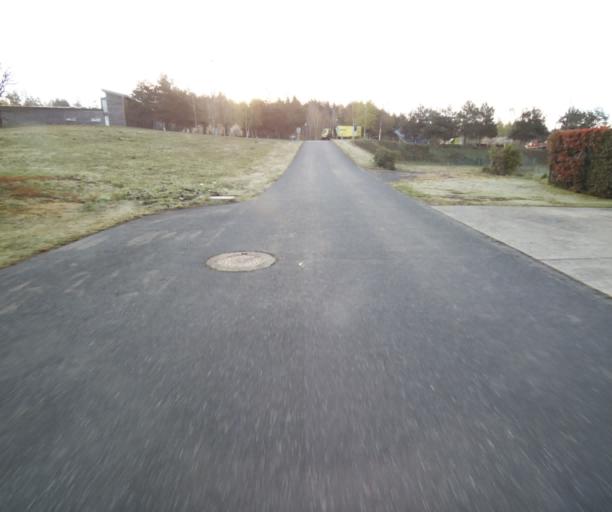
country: FR
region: Limousin
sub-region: Departement de la Correze
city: Correze
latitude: 45.3185
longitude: 1.8482
